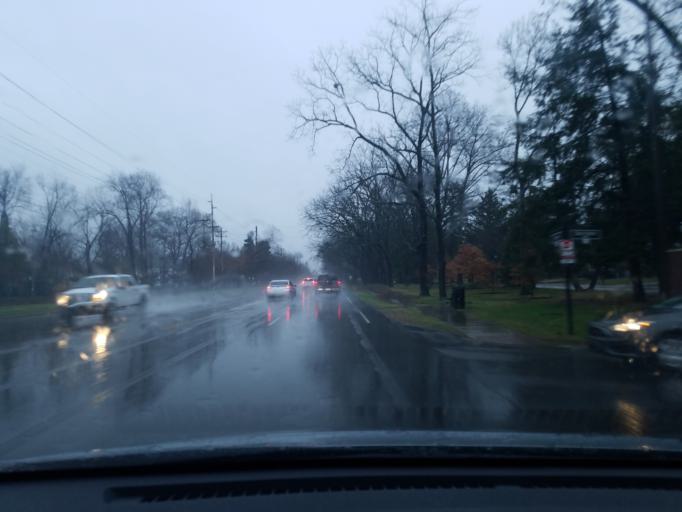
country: US
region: Kentucky
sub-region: Jefferson County
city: Lyndon
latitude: 38.2478
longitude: -85.5946
